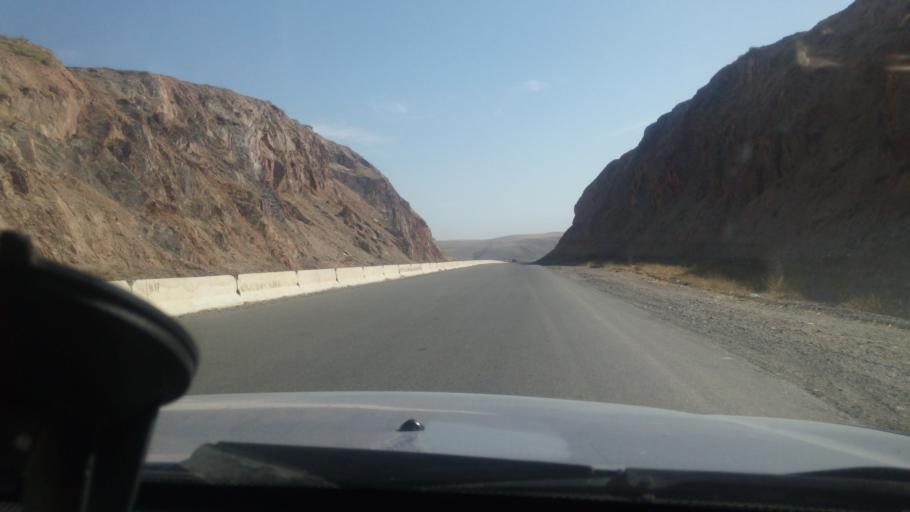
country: UZ
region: Jizzax
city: Jizzax
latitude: 40.0491
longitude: 67.6790
